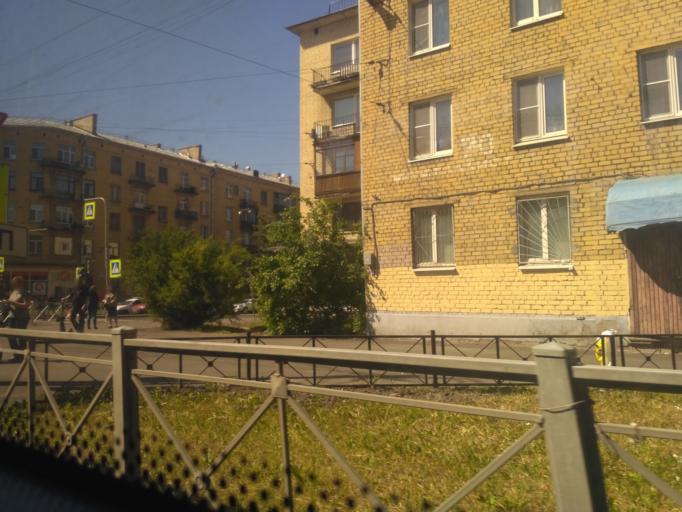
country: RU
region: Leningrad
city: Kalininskiy
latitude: 59.9599
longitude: 30.4222
